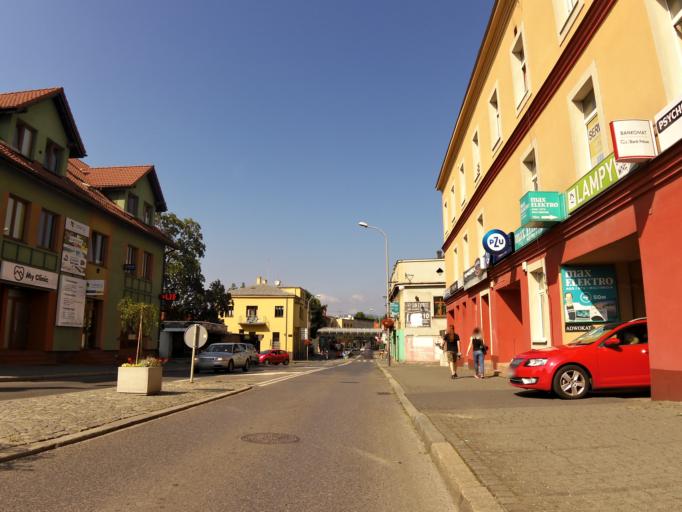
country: PL
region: Silesian Voivodeship
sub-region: Powiat zywiecki
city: Zywiec
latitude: 49.6827
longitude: 19.1896
